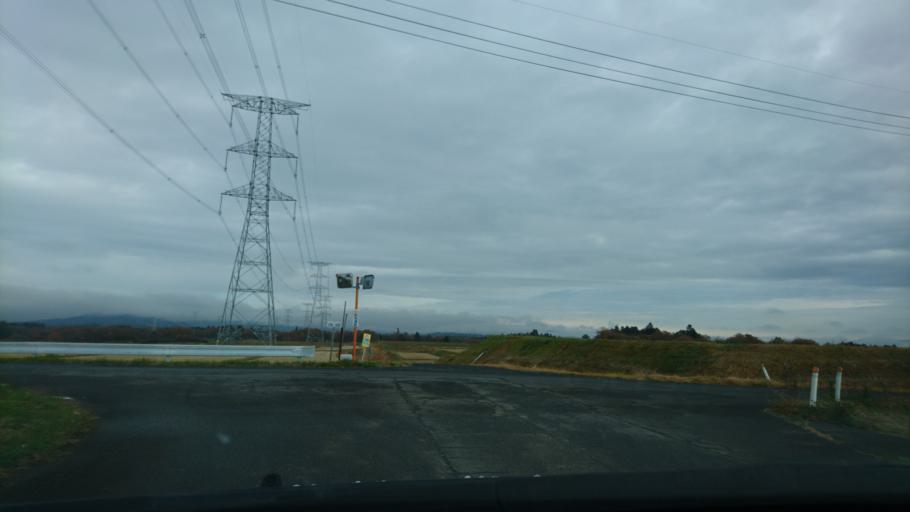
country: JP
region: Iwate
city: Ichinoseki
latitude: 38.8859
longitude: 141.1945
